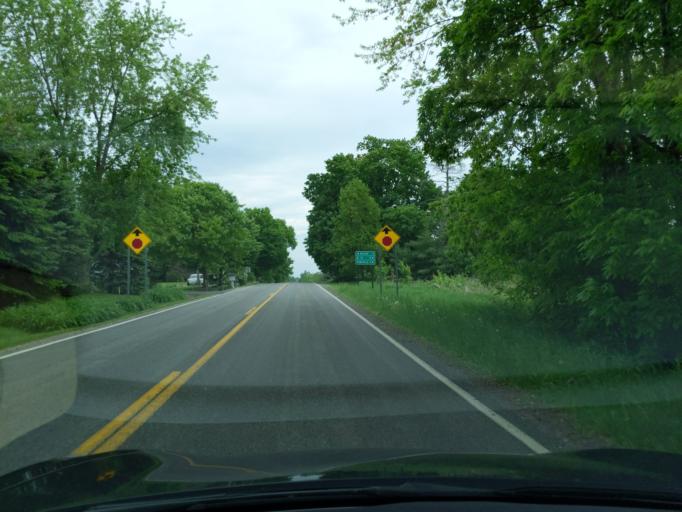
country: US
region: Michigan
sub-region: Ingham County
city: Mason
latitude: 42.5539
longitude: -84.3567
